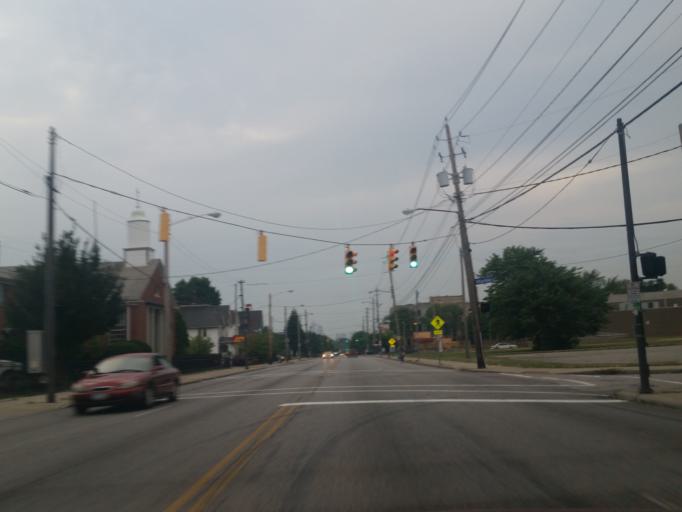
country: US
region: Ohio
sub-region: Cuyahoga County
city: Newburgh Heights
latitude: 41.4554
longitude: -81.6354
